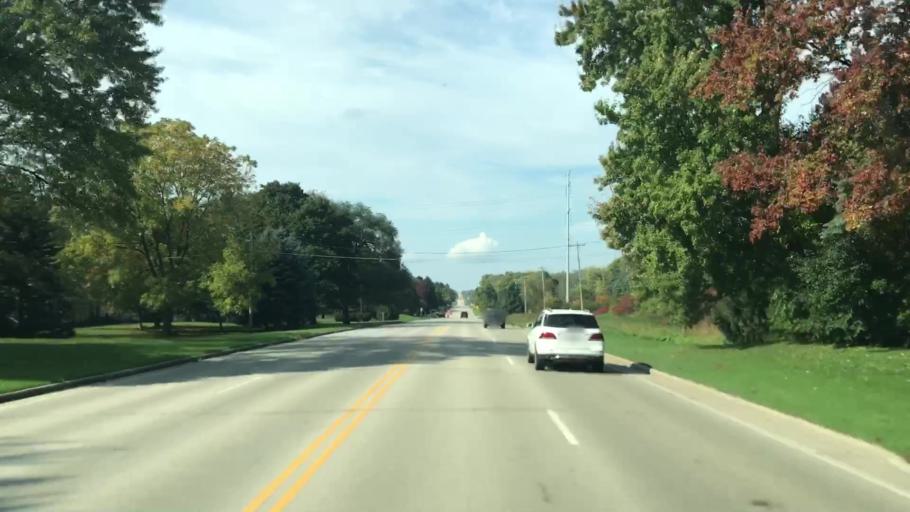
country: US
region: Wisconsin
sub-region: Ozaukee County
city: Mequon
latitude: 43.2217
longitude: -88.0108
